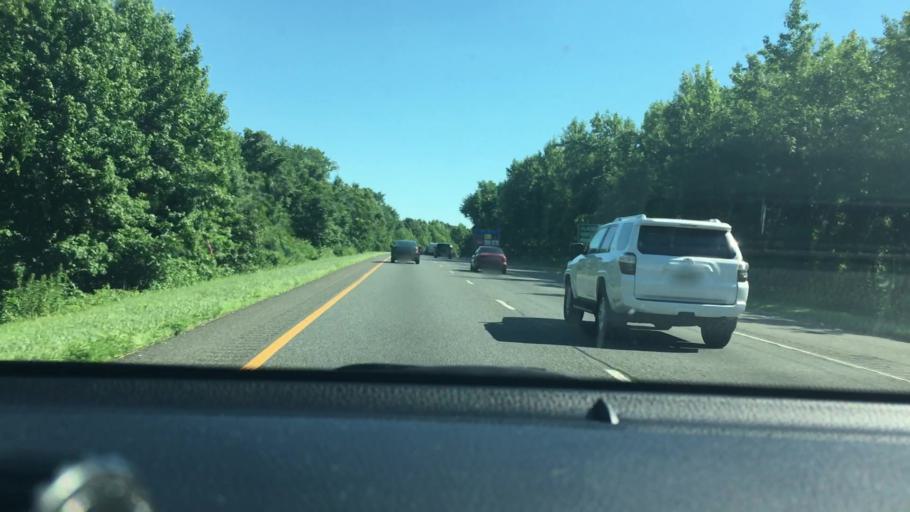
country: US
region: New Jersey
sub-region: Camden County
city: Glendora
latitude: 39.8418
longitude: -75.0979
